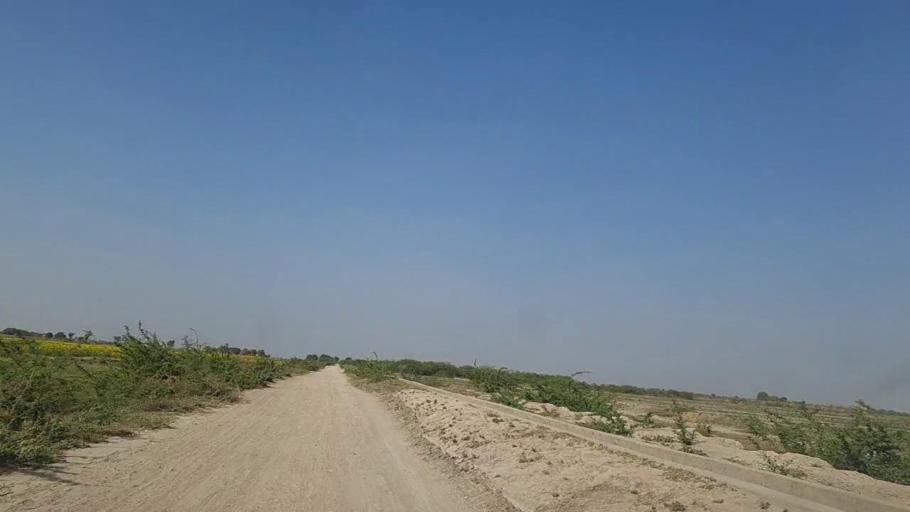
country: PK
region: Sindh
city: Naukot
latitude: 24.9011
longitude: 69.4875
